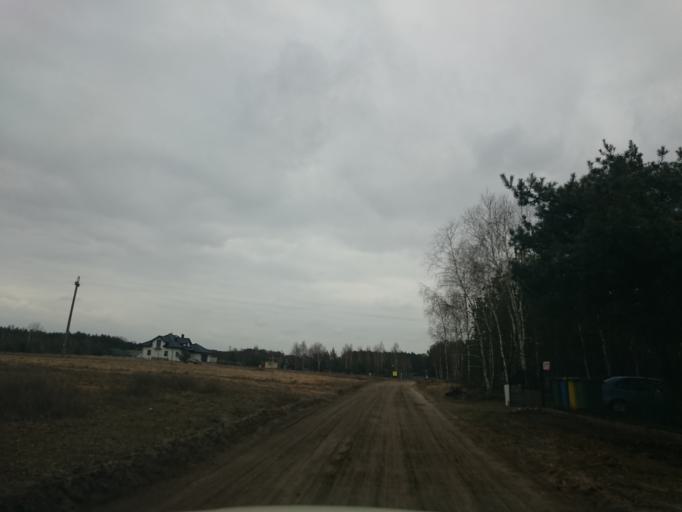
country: PL
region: Kujawsko-Pomorskie
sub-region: Powiat golubsko-dobrzynski
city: Ciechocin
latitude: 53.0493
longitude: 18.8708
